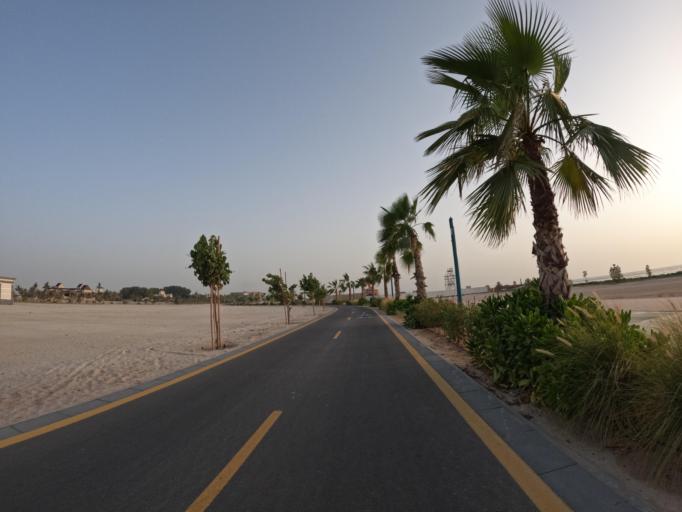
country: AE
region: Dubai
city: Dubai
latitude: 25.1918
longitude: 55.2284
